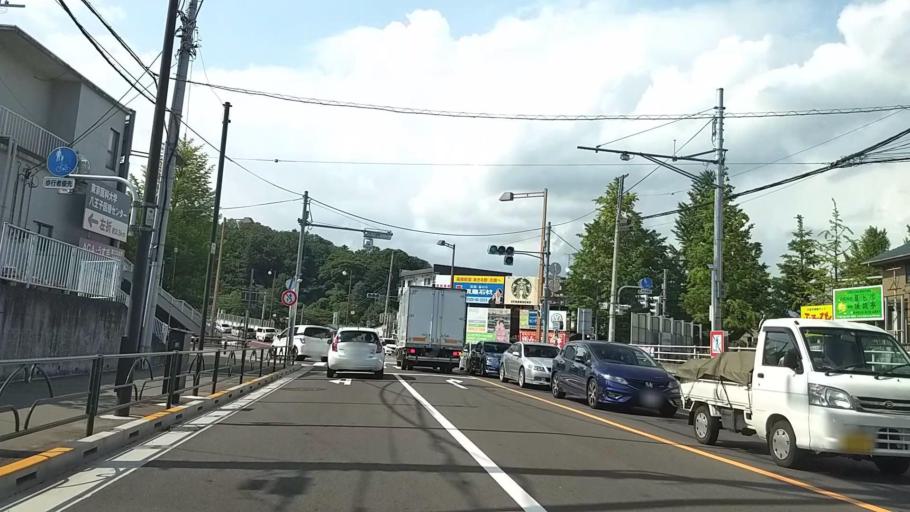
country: JP
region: Tokyo
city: Hachioji
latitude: 35.6445
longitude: 139.2853
